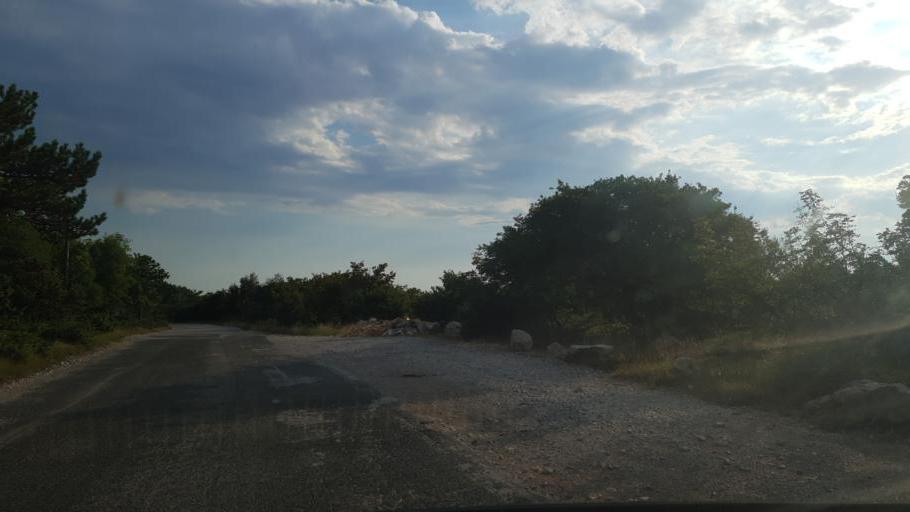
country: HR
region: Primorsko-Goranska
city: Omisalj
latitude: 45.2279
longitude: 14.5735
